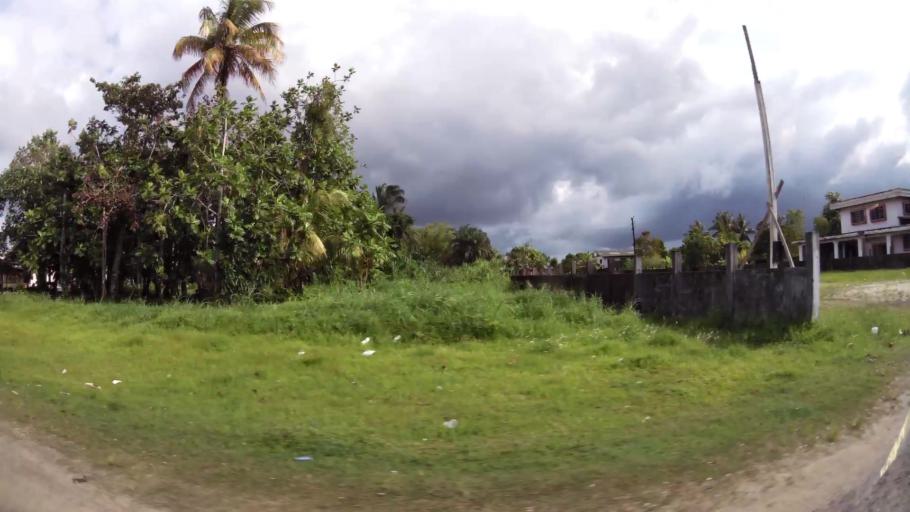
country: SR
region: Paramaribo
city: Paramaribo
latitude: 5.8428
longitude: -55.2102
